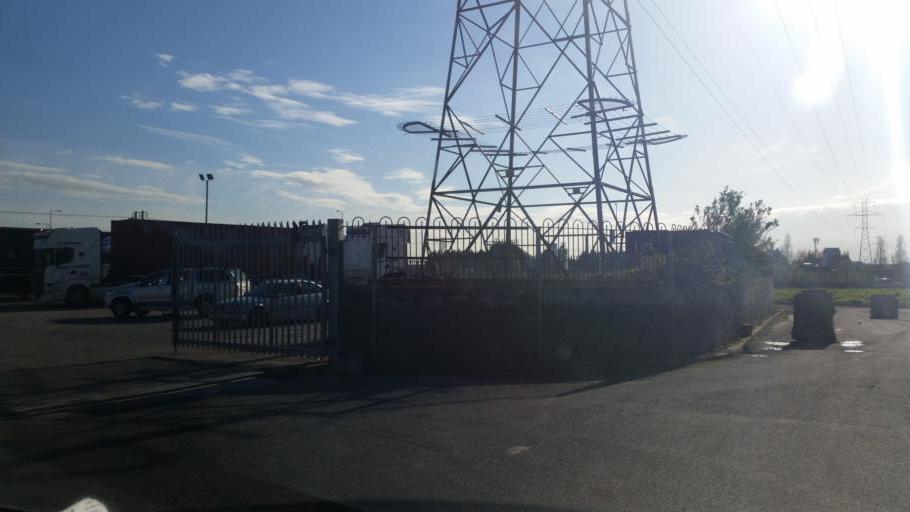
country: IE
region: Leinster
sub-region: Fingal County
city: Blanchardstown
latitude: 53.4070
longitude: -6.3424
